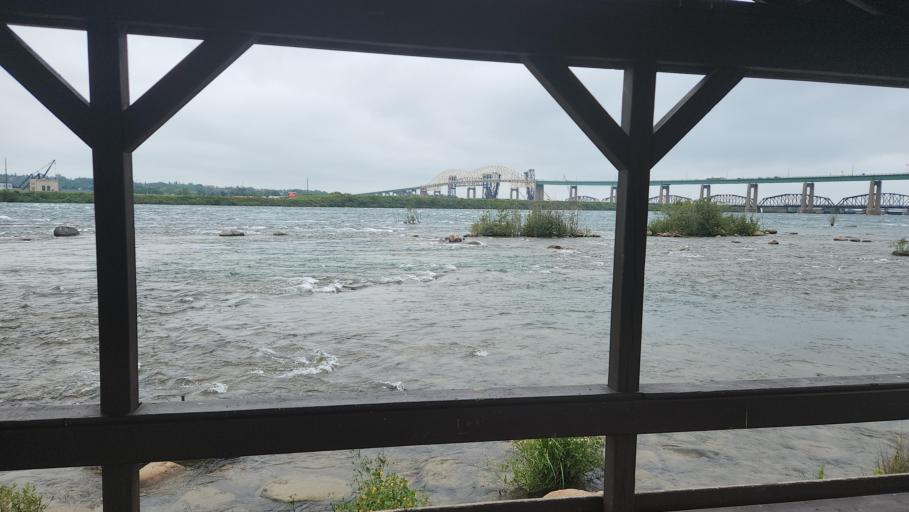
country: US
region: Michigan
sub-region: Chippewa County
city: Sault Ste. Marie
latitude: 46.5093
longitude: -84.3535
